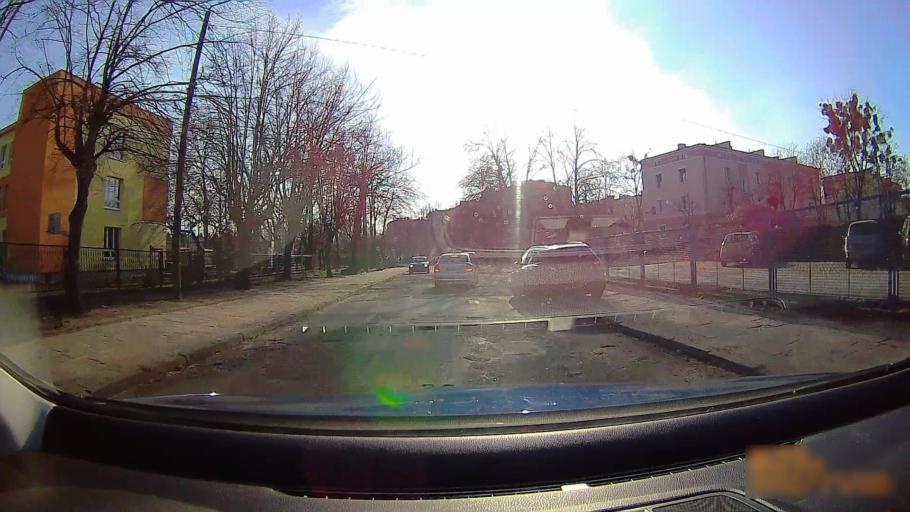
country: PL
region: Greater Poland Voivodeship
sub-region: Konin
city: Konin
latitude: 52.2294
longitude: 18.2594
